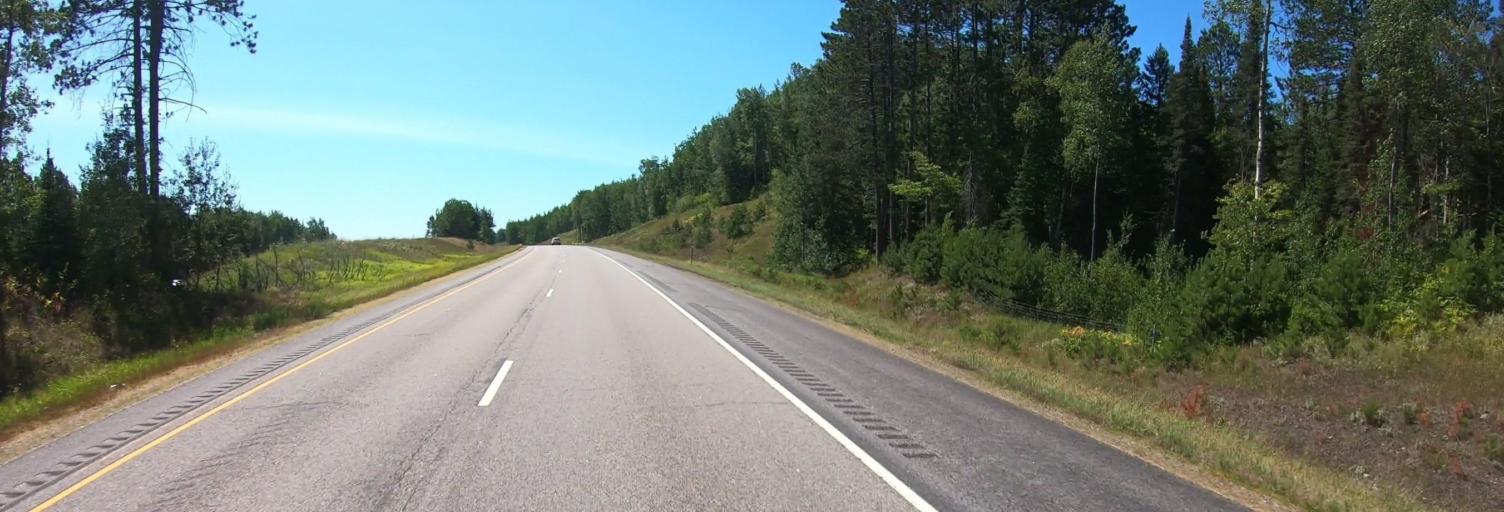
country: US
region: Minnesota
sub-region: Saint Louis County
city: Mountain Iron
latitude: 47.6827
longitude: -92.6533
